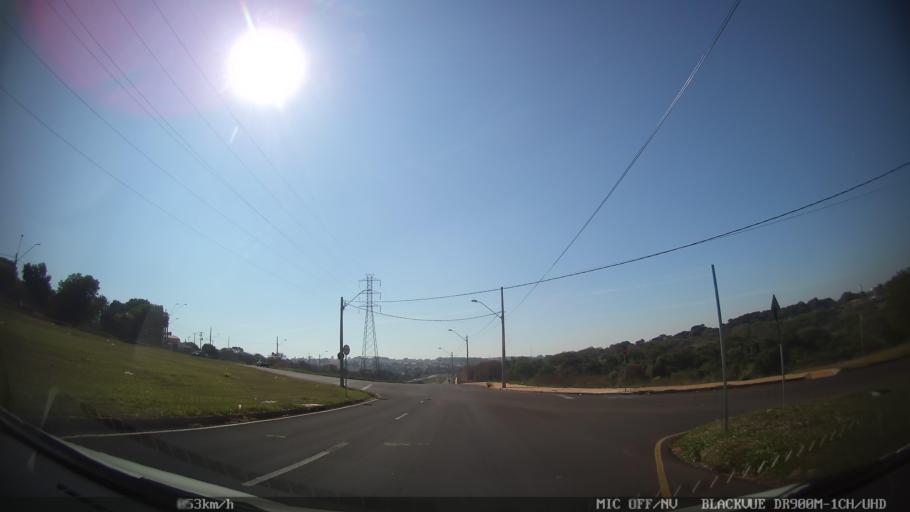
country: BR
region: Sao Paulo
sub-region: Sao Jose Do Rio Preto
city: Sao Jose do Rio Preto
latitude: -20.7639
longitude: -49.3777
